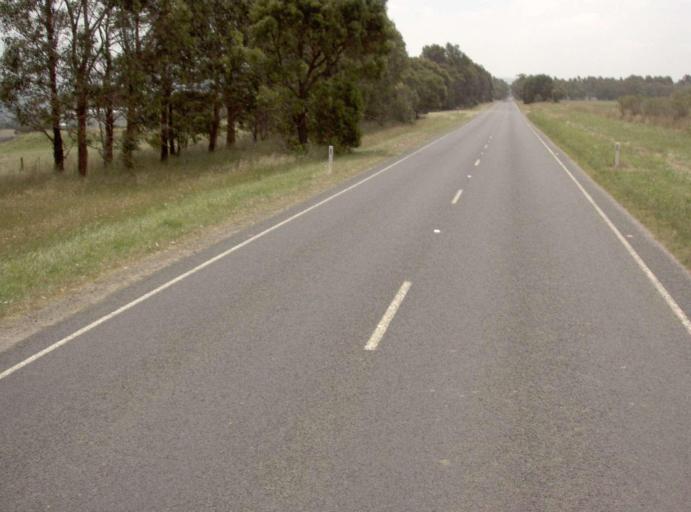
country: AU
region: Victoria
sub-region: Latrobe
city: Traralgon
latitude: -38.4966
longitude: 146.7120
